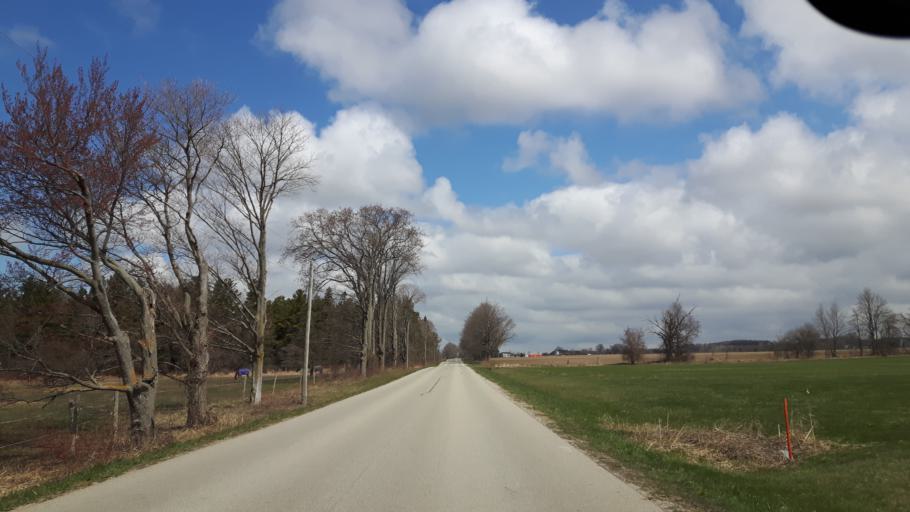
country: CA
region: Ontario
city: Goderich
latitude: 43.6302
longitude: -81.6846
